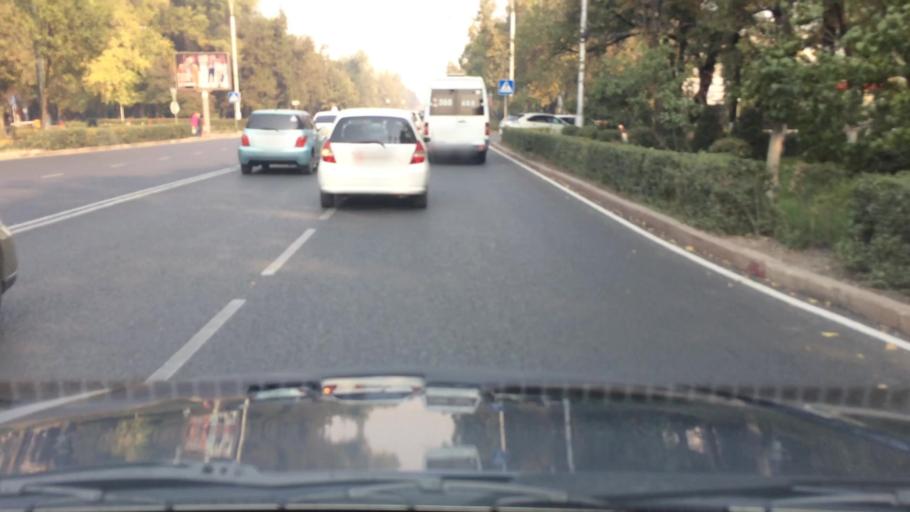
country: KG
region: Chuy
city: Bishkek
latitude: 42.8445
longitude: 74.5862
